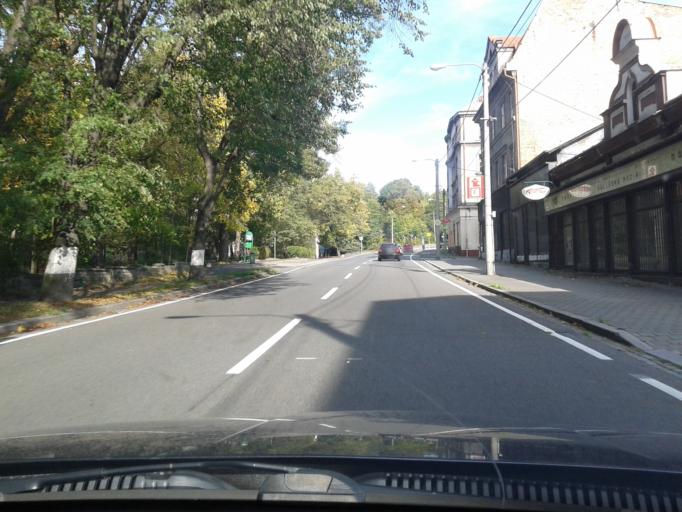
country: CZ
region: Moravskoslezsky
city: Orlova
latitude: 49.8459
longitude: 18.4326
